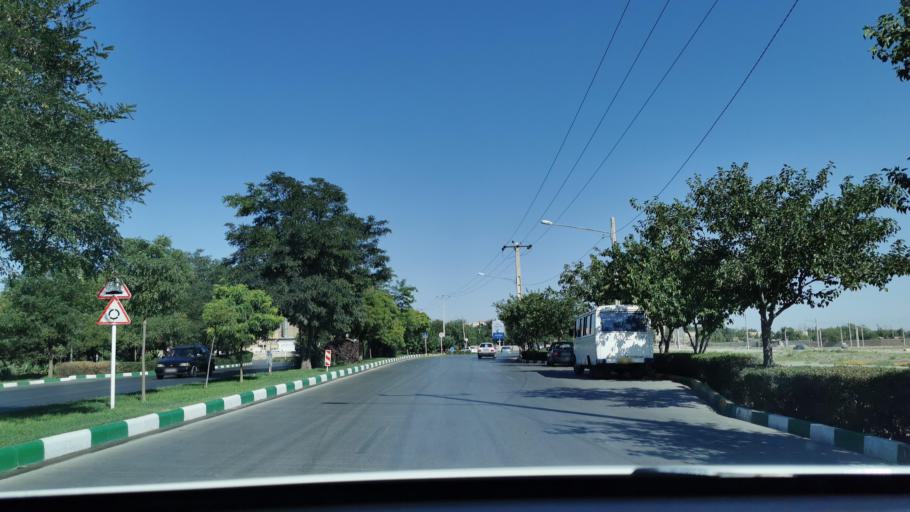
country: IR
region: Razavi Khorasan
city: Mashhad
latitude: 36.3314
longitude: 59.6440
